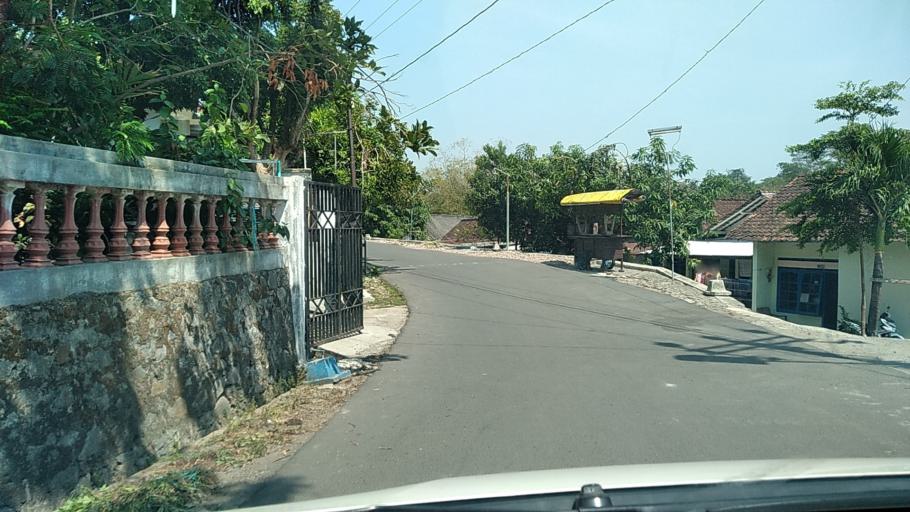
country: ID
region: Central Java
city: Semarang
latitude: -7.0361
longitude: 110.4158
